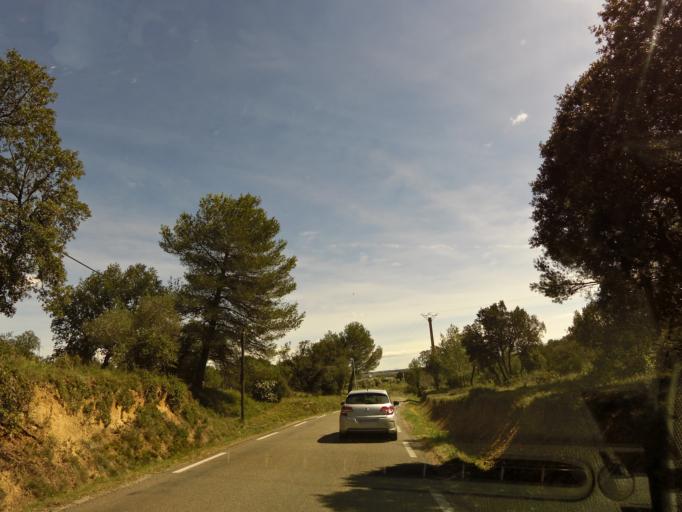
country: FR
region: Languedoc-Roussillon
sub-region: Departement du Gard
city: Bernis
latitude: 43.7783
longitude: 4.2785
